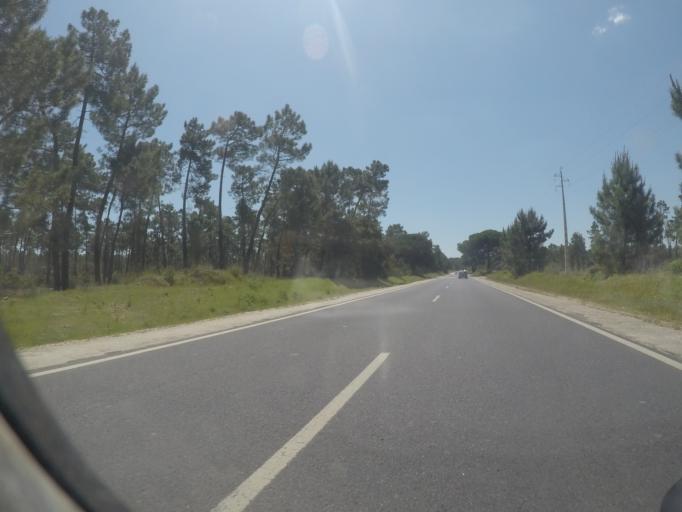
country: PT
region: Setubal
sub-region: Sesimbra
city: Sesimbra
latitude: 38.5279
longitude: -9.1012
